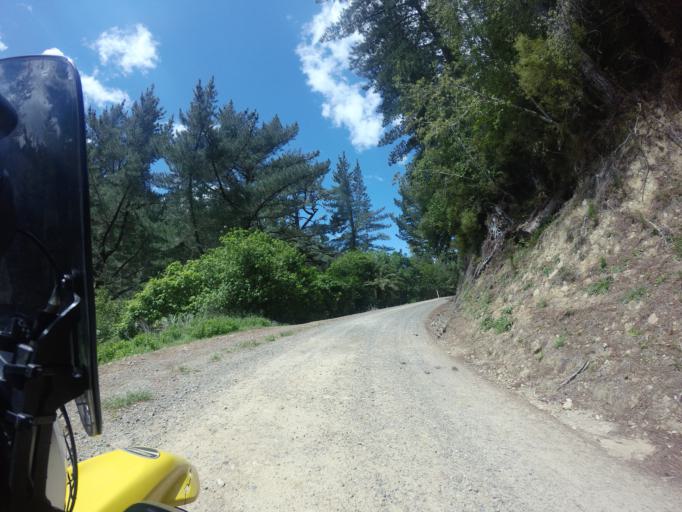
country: NZ
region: Hawke's Bay
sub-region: Wairoa District
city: Wairoa
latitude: -38.9713
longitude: 177.6836
